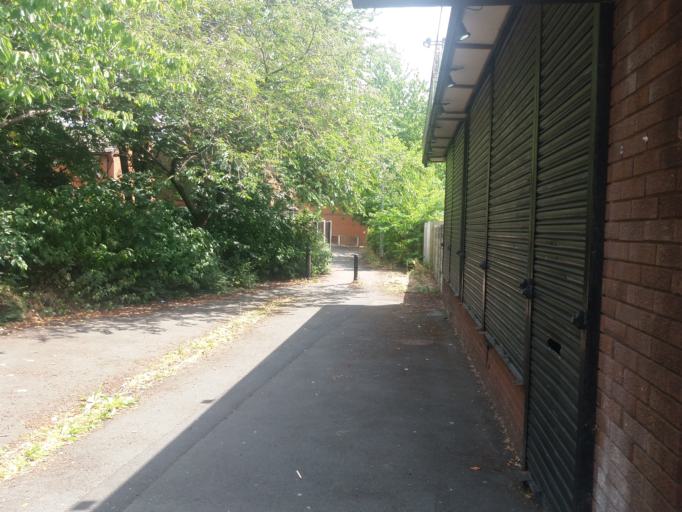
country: GB
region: England
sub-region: Lancashire
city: Preston
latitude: 53.7541
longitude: -2.7156
